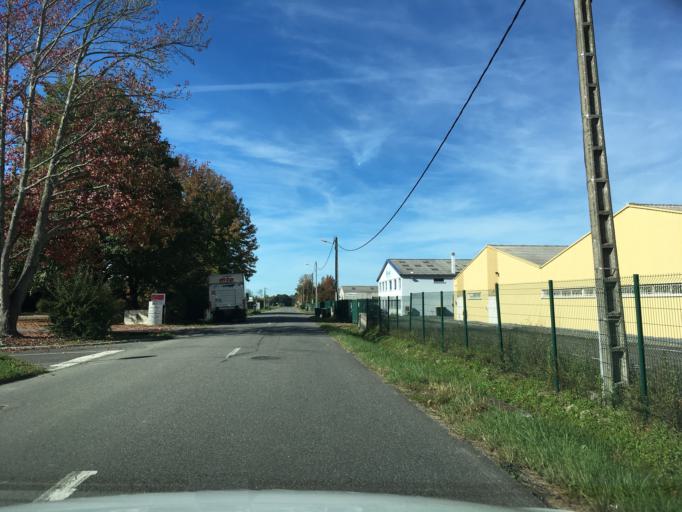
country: FR
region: Aquitaine
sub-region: Departement des Pyrenees-Atlantiques
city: Buros
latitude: 43.3251
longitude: -0.3008
